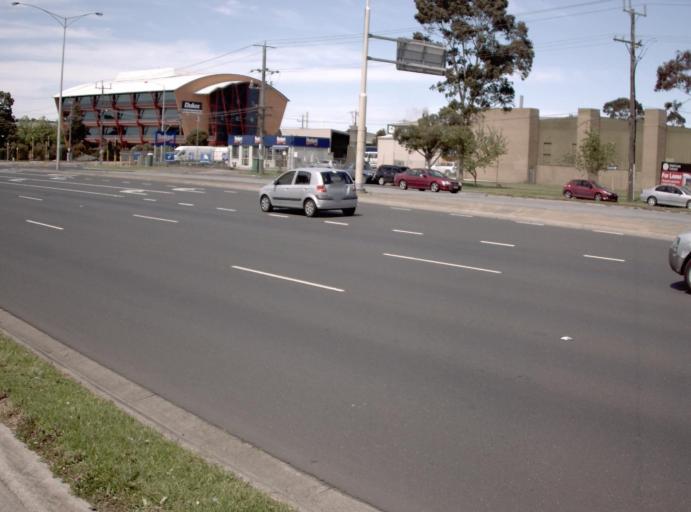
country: AU
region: Victoria
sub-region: Monash
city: Clayton
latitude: -37.9224
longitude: 145.1404
